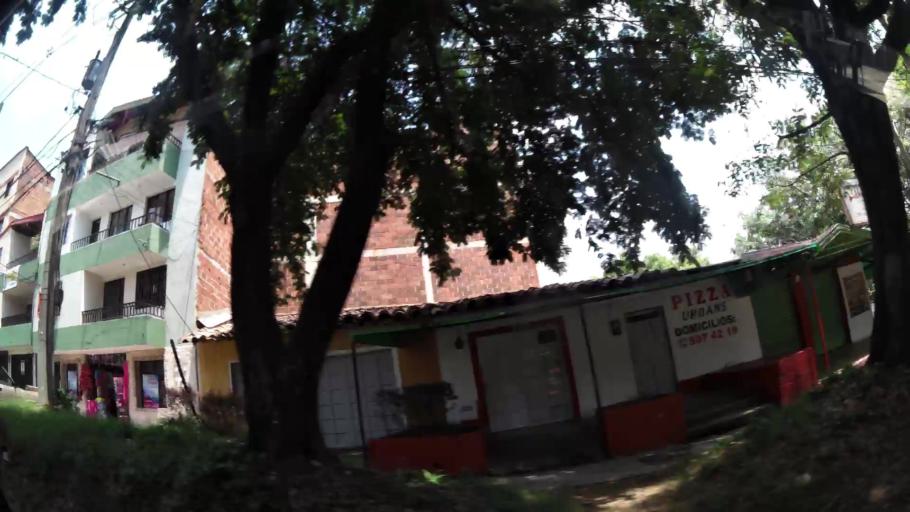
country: CO
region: Antioquia
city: Medellin
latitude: 6.2359
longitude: -75.6072
